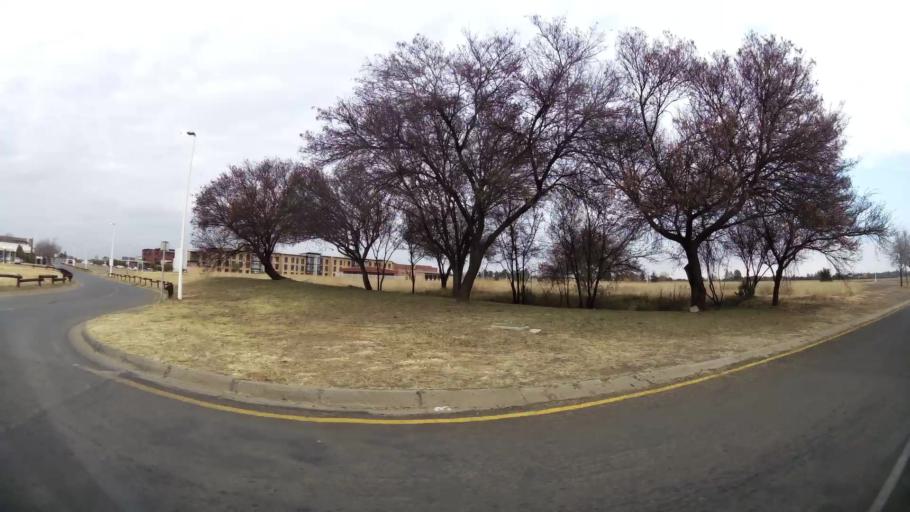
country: ZA
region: Orange Free State
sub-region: Mangaung Metropolitan Municipality
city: Bloemfontein
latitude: -29.1063
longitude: 26.1822
